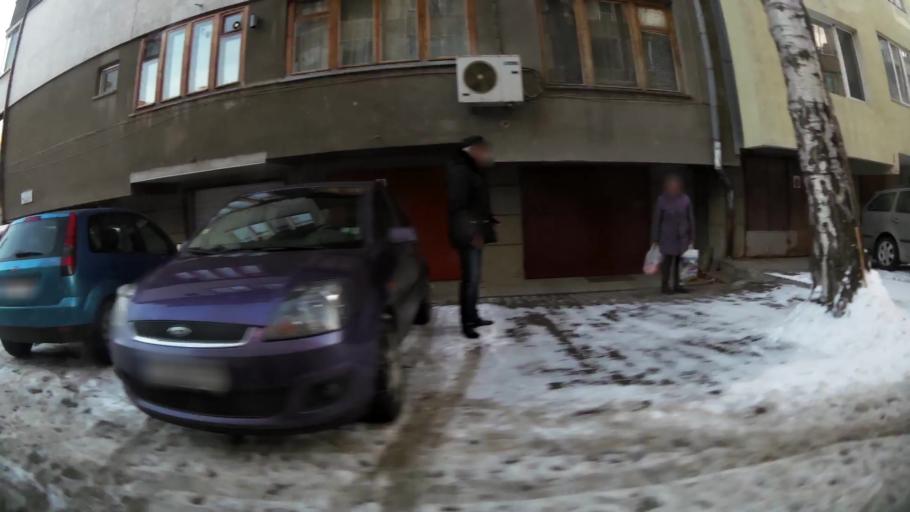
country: BG
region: Sofia-Capital
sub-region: Stolichna Obshtina
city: Sofia
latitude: 42.6853
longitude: 23.3608
